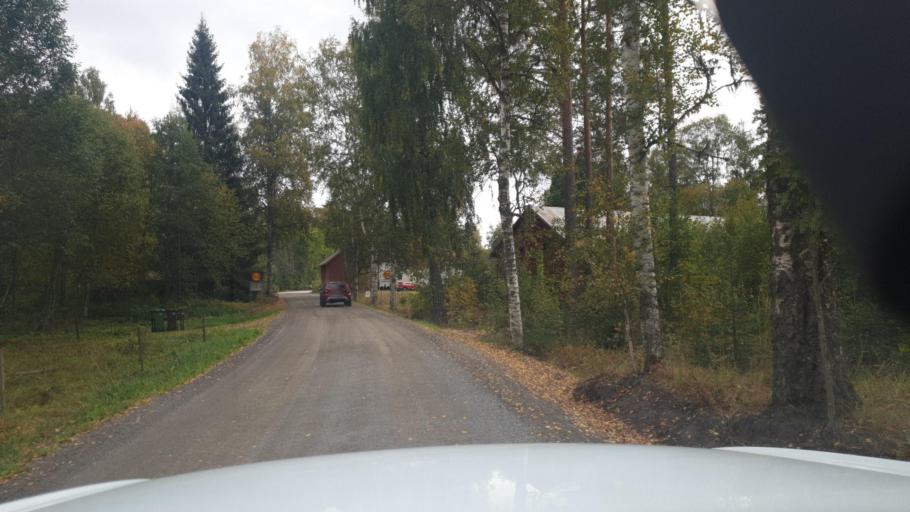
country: SE
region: Vaermland
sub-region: Torsby Kommun
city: Torsby
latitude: 59.9459
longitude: 12.9021
